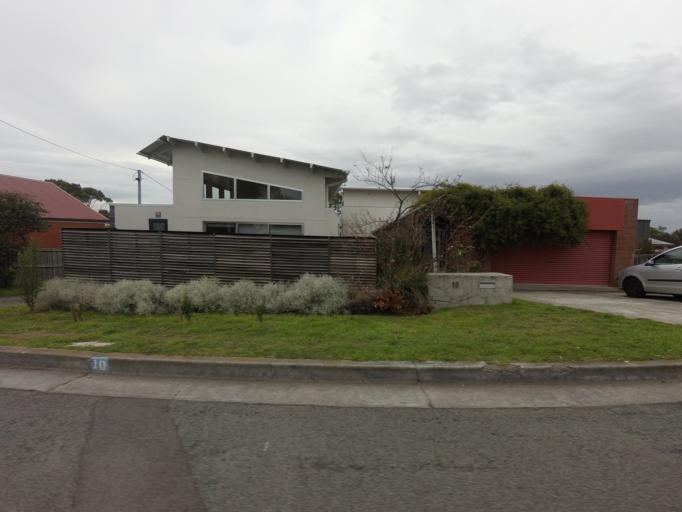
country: AU
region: Tasmania
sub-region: Clarence
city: Bellerive
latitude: -42.8801
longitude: 147.3682
